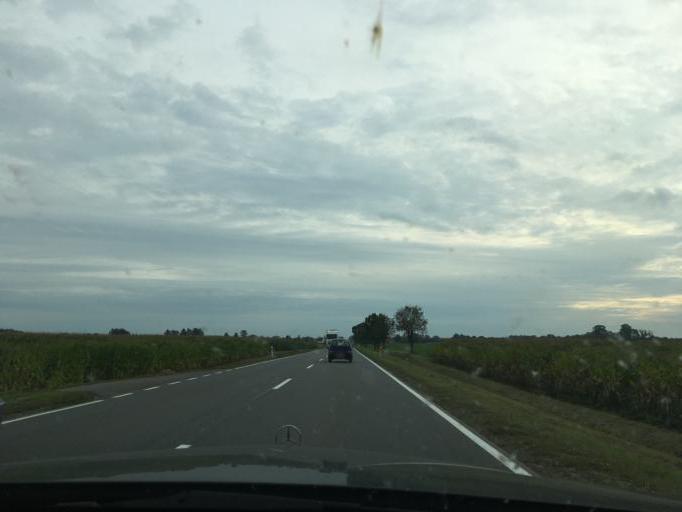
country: PL
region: Masovian Voivodeship
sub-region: Powiat ostrolecki
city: Czerwin
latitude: 52.9455
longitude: 21.8873
